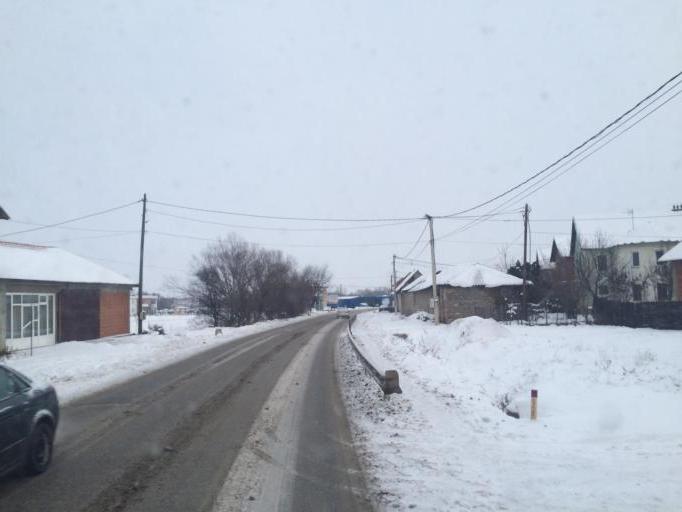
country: XK
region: Pristina
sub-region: Komuna e Drenasit
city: Glogovac
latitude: 42.5876
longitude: 20.8942
